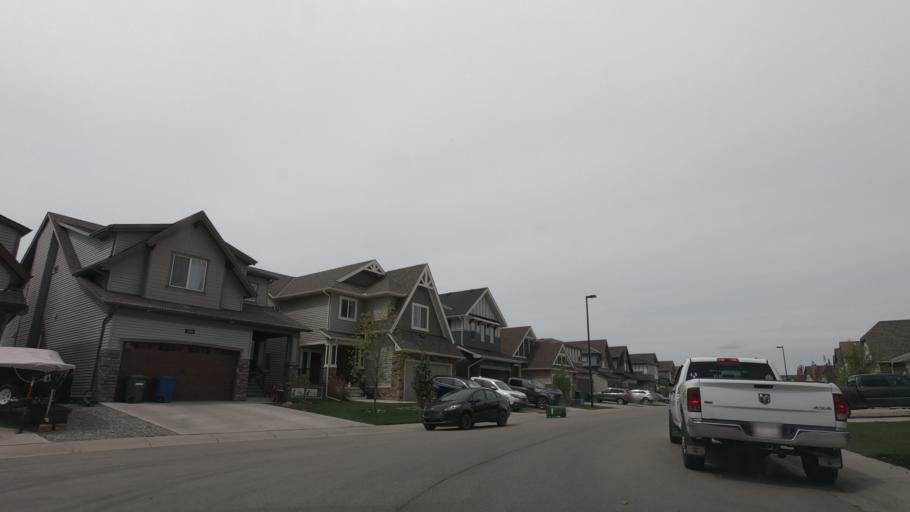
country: CA
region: Alberta
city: Airdrie
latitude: 51.3054
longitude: -114.0410
